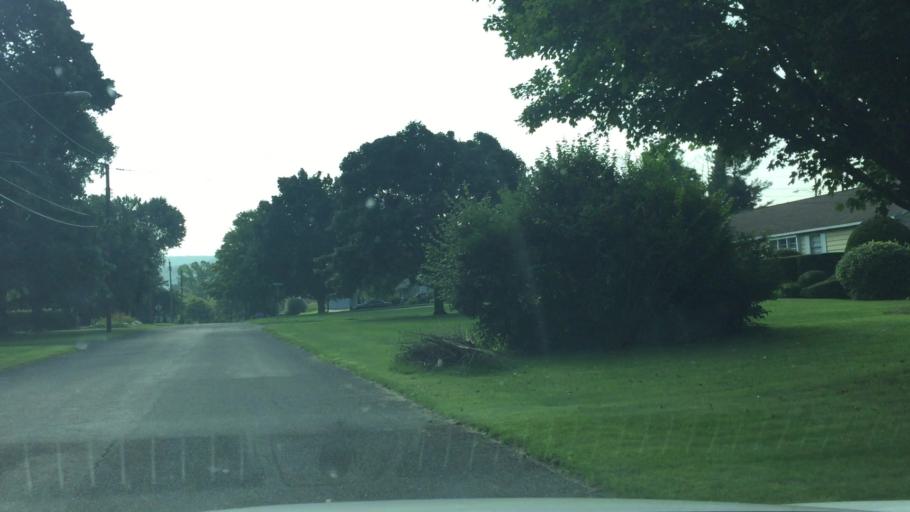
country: US
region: Massachusetts
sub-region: Berkshire County
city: Pittsfield
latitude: 42.4296
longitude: -73.2107
